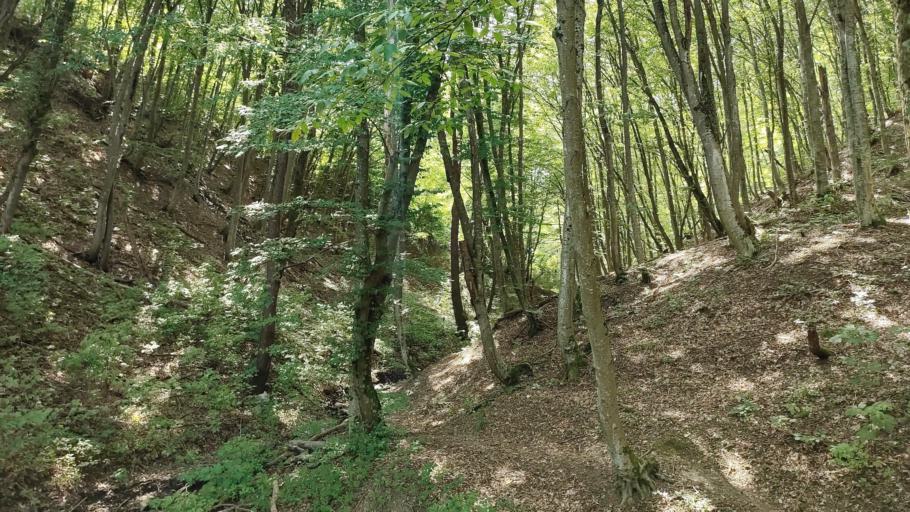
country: RU
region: Krasnodarskiy
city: Goryachiy Klyuch
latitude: 44.6204
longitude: 39.1069
